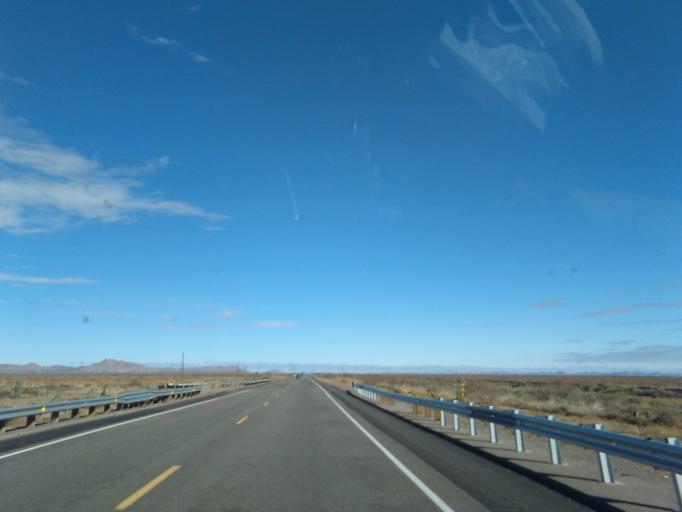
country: US
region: New Mexico
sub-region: Luna County
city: Deming
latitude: 32.3047
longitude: -107.7005
